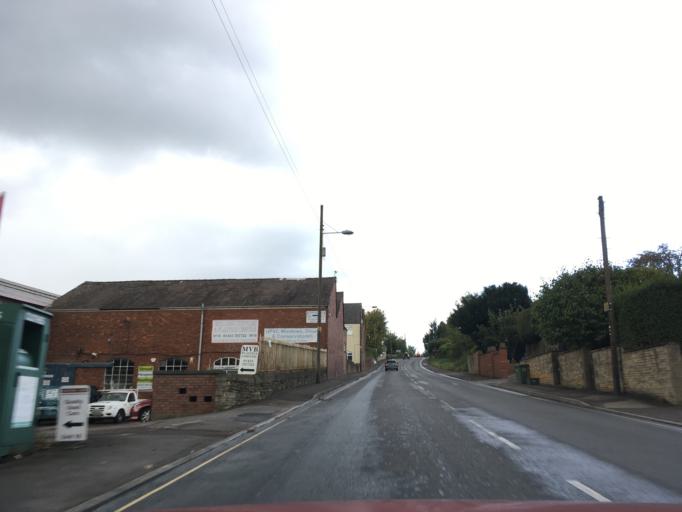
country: GB
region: England
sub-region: Gloucestershire
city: Stroud
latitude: 51.7358
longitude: -2.2327
